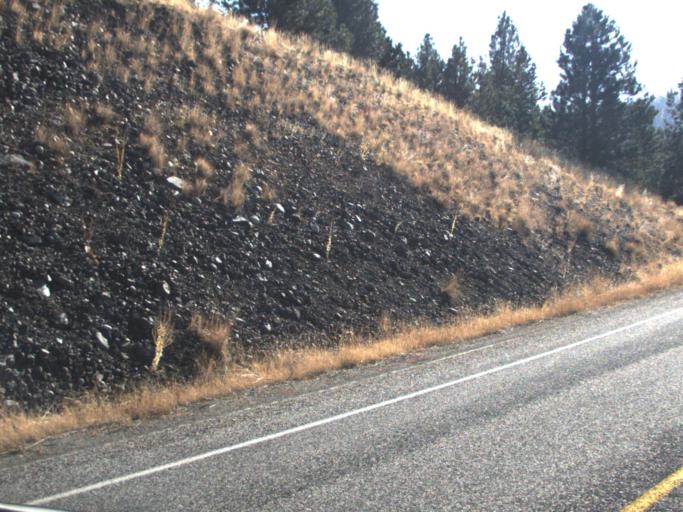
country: US
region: Washington
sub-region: Ferry County
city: Republic
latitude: 48.6636
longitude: -118.6664
